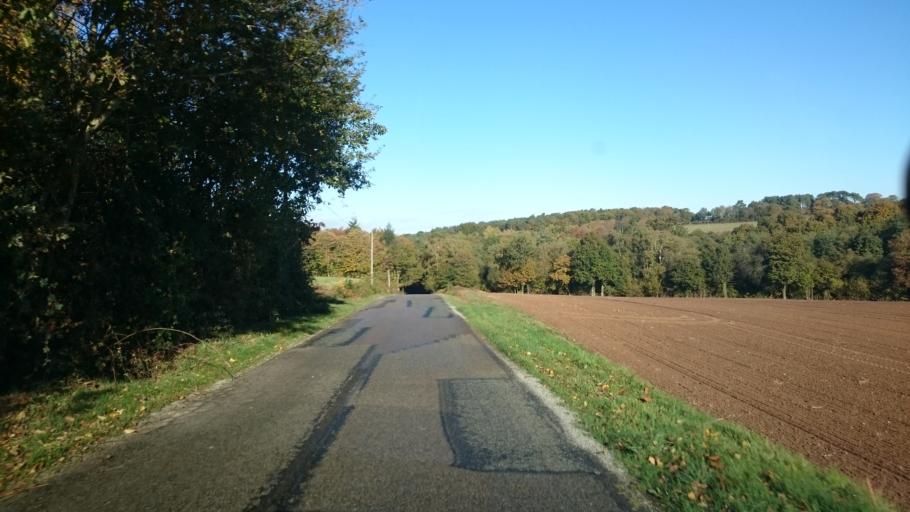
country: FR
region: Brittany
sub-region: Departement d'Ille-et-Vilaine
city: Laille
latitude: 47.9604
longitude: -1.7035
